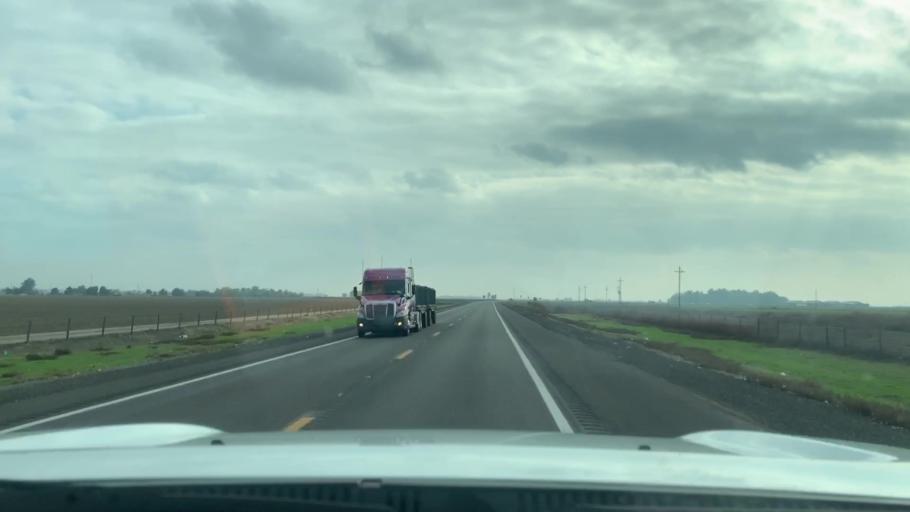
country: US
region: California
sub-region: Kings County
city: Lemoore
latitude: 36.2625
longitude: -119.8077
